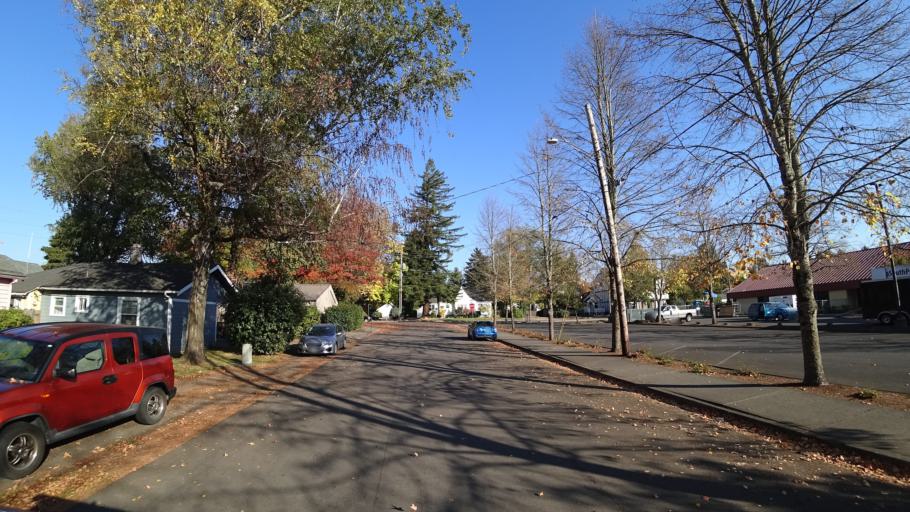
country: US
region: Oregon
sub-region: Multnomah County
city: Gresham
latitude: 45.5030
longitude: -122.4318
